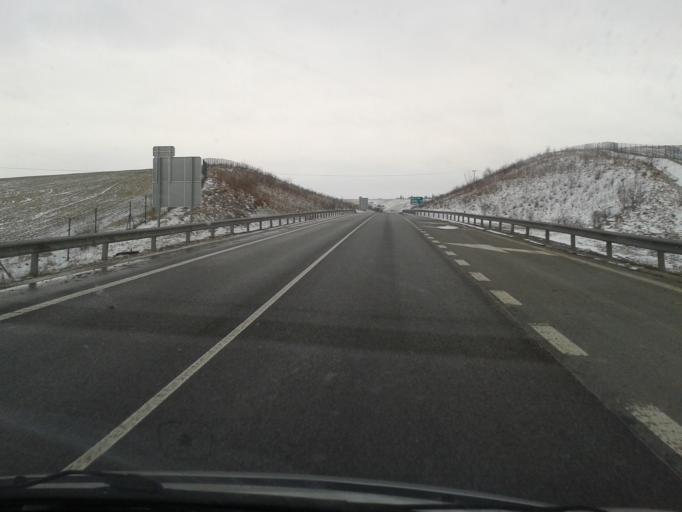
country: SK
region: Zilinsky
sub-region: Okres Zilina
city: Trstena
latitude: 49.3657
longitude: 19.6330
